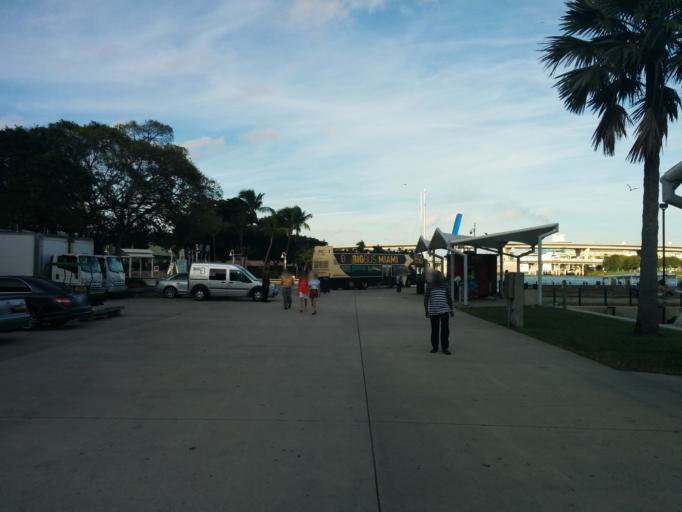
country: US
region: Florida
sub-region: Miami-Dade County
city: Miami
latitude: 25.7761
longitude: -80.1848
